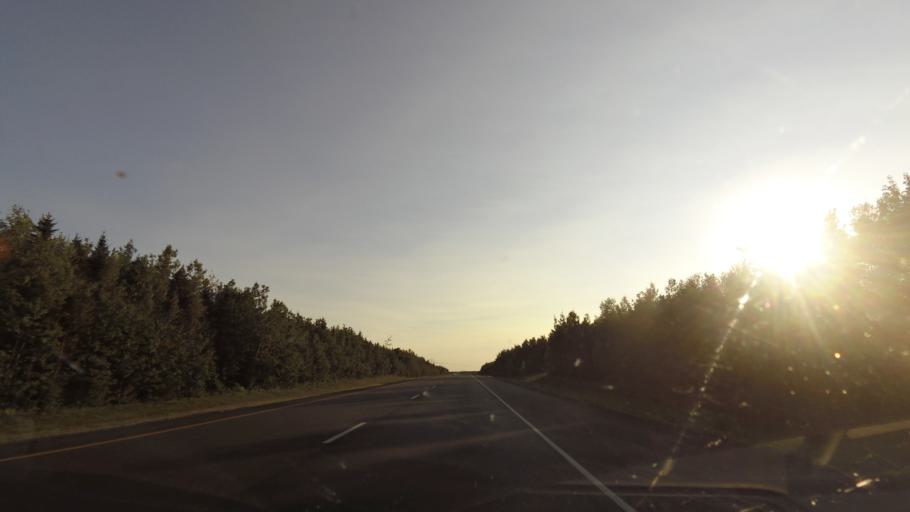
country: CA
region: New Brunswick
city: Salisbury
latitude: 46.0918
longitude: -64.9383
